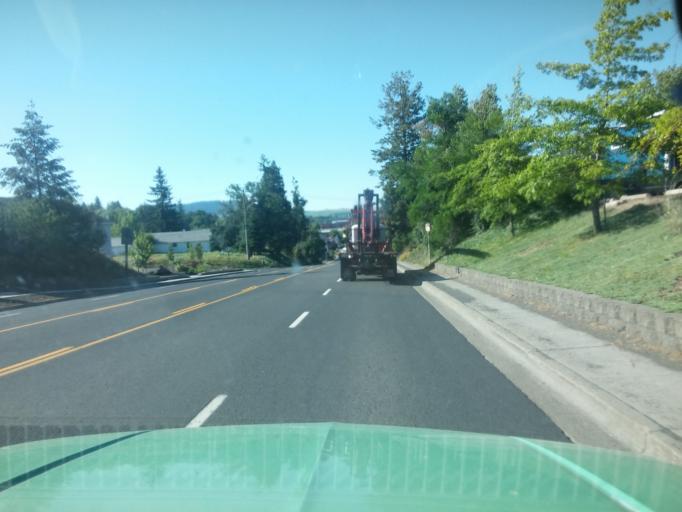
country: US
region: Idaho
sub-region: Latah County
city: Moscow
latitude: 46.7406
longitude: -117.0016
